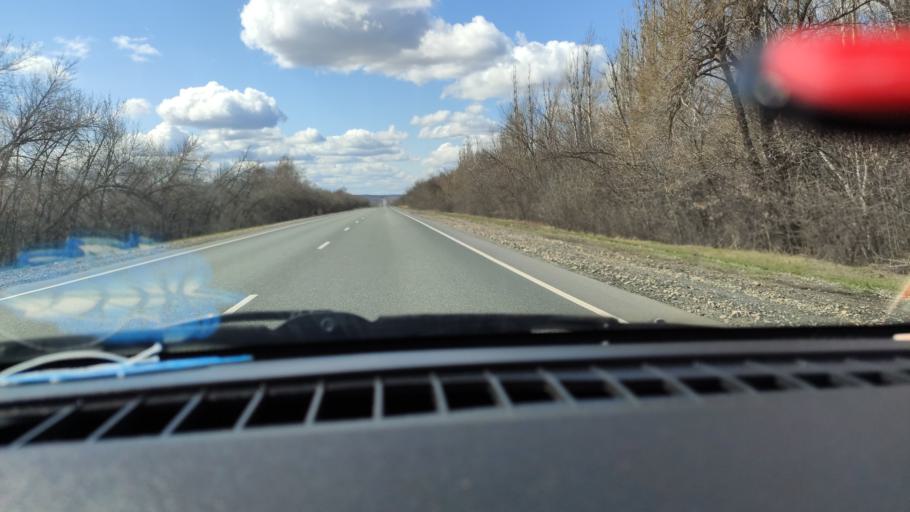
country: RU
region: Saratov
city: Khvalynsk
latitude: 52.5943
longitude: 48.1351
